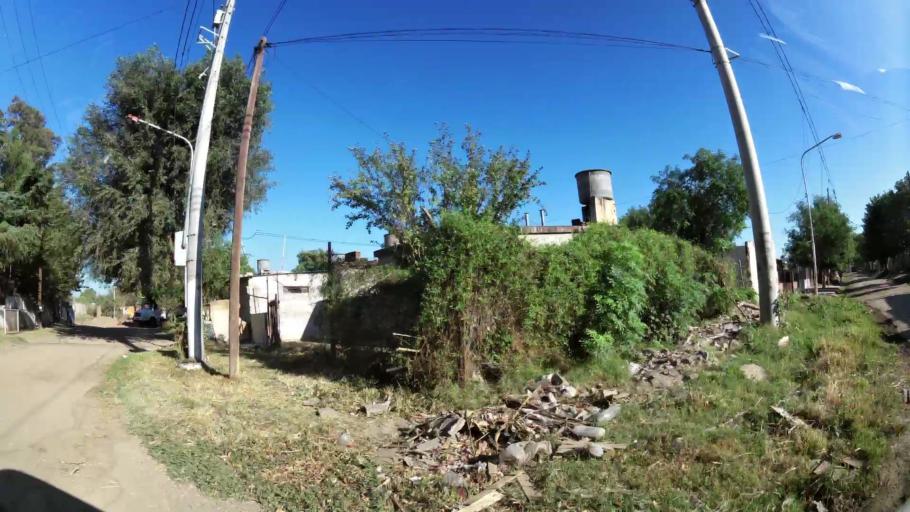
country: AR
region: Cordoba
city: Villa Allende
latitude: -31.3319
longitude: -64.2410
